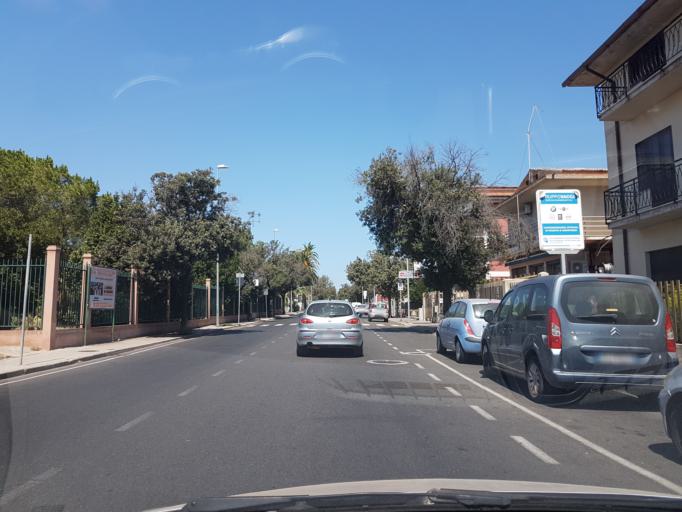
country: IT
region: Sardinia
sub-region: Provincia di Oristano
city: Oristano
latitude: 39.8936
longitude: 8.5977
